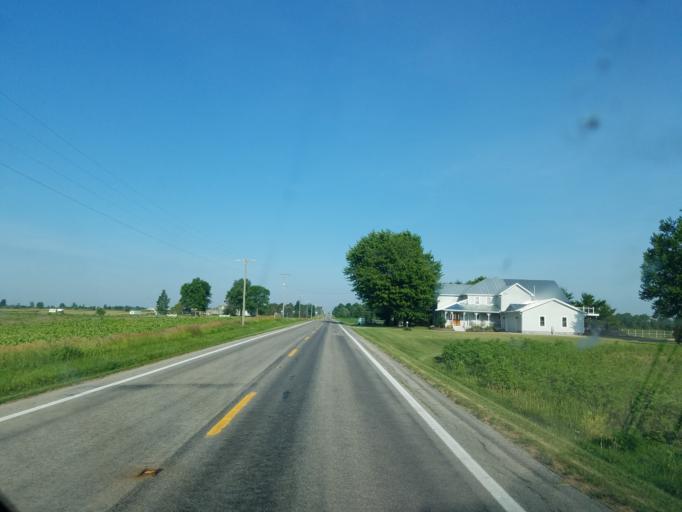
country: US
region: Ohio
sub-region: Hardin County
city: Kenton
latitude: 40.7317
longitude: -83.6319
